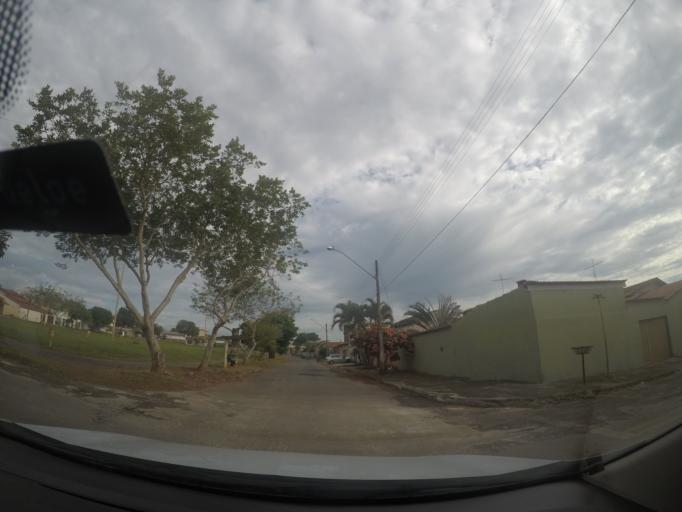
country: BR
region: Goias
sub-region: Goiania
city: Goiania
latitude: -16.6862
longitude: -49.1990
